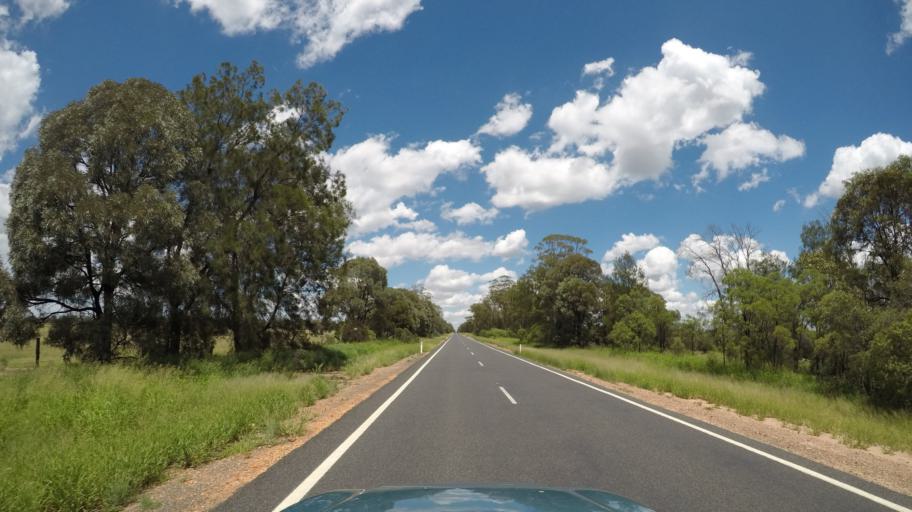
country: AU
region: Queensland
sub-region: Goondiwindi
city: Goondiwindi
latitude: -28.0119
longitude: 150.8740
